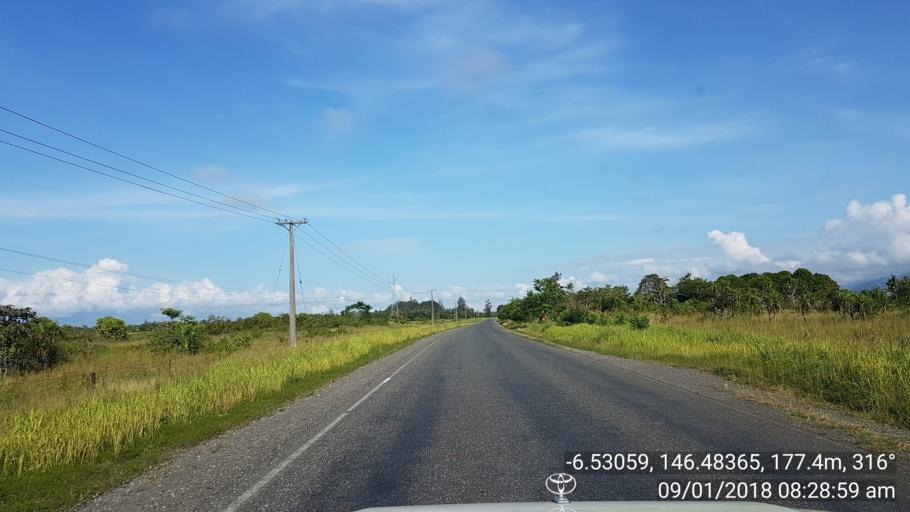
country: PG
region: Morobe
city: Lae
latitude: -6.5308
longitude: 146.4839
